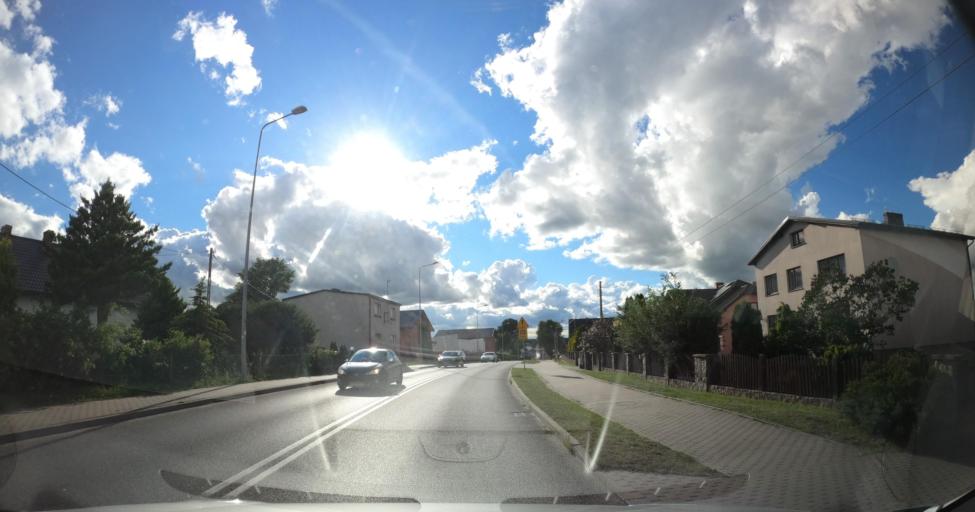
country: PL
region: Pomeranian Voivodeship
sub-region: Powiat kartuski
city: Przodkowo
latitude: 54.3149
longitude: 18.2735
